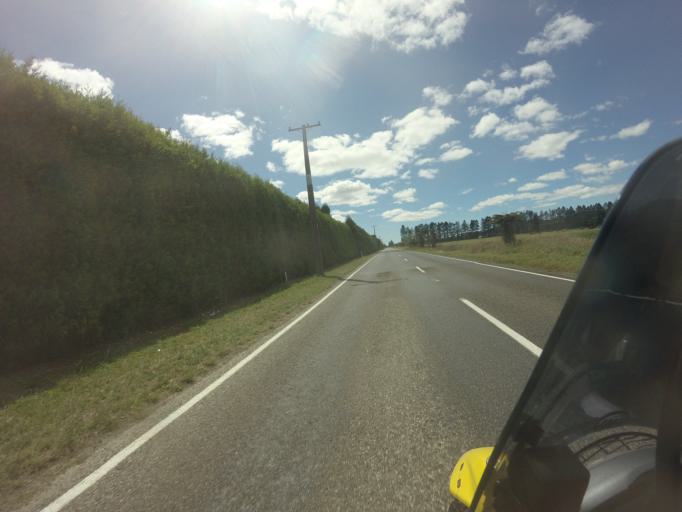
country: NZ
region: Bay of Plenty
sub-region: Whakatane District
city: Edgecumbe
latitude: -38.0501
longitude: 176.8286
